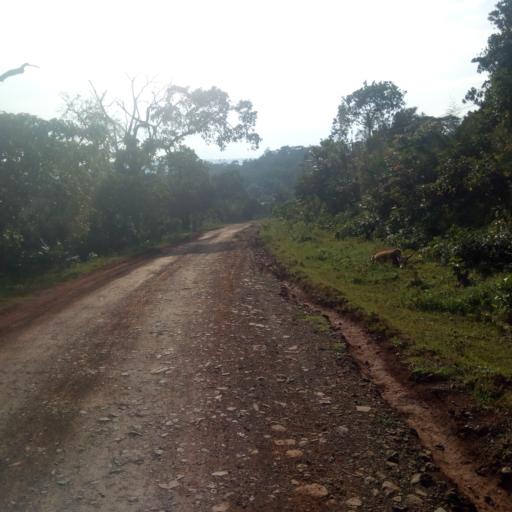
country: ET
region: Oromiya
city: Gore
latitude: 7.8758
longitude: 35.4818
